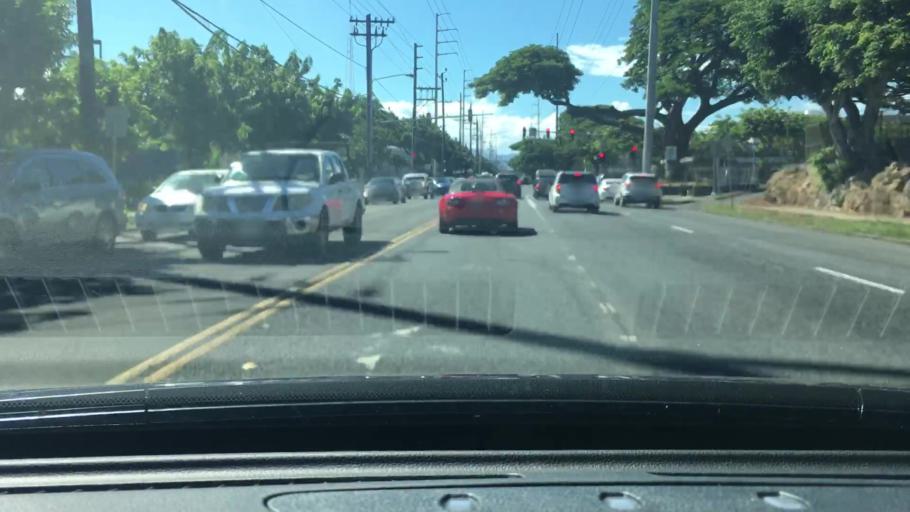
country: US
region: Hawaii
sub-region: Honolulu County
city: Honolulu
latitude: 21.3189
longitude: -157.8677
